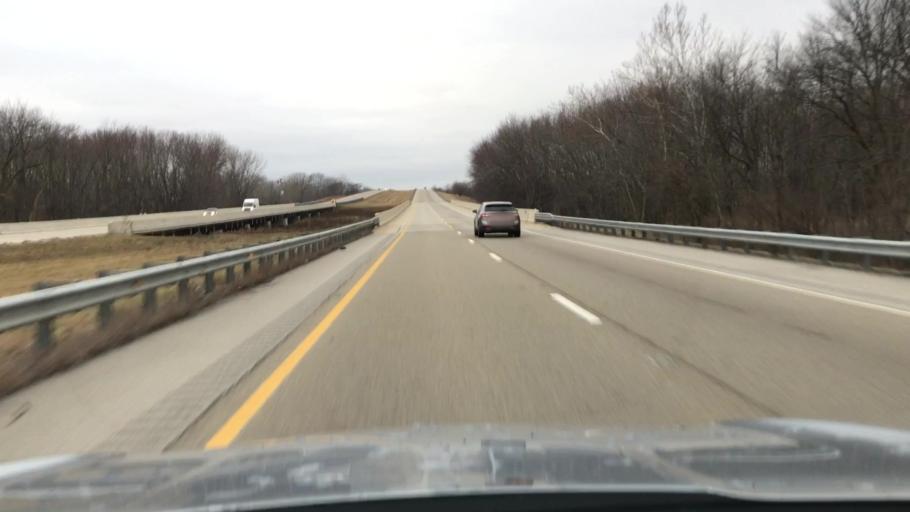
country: US
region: Illinois
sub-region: Logan County
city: Lincoln
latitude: 40.1818
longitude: -89.3683
